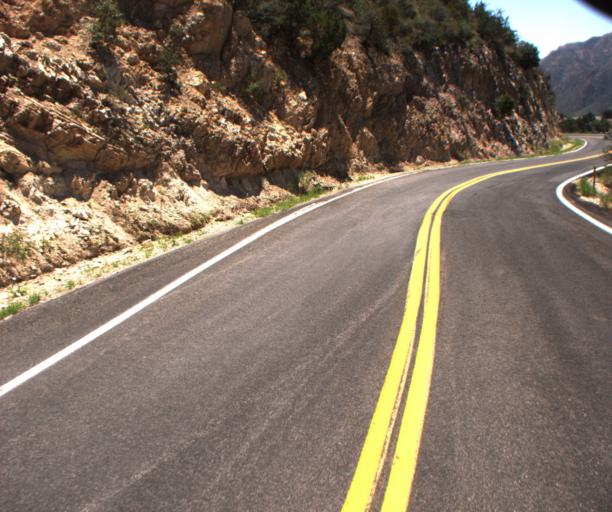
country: US
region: Arizona
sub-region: Greenlee County
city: Morenci
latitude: 33.1673
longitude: -109.3657
